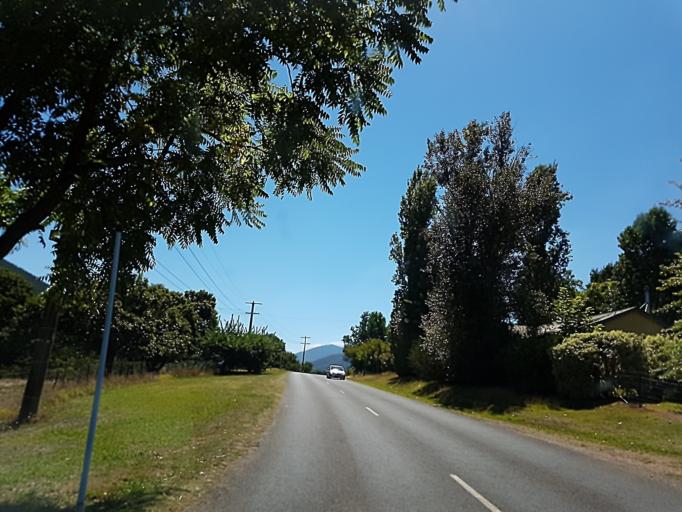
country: AU
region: Victoria
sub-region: Alpine
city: Mount Beauty
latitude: -36.7603
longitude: 146.9835
